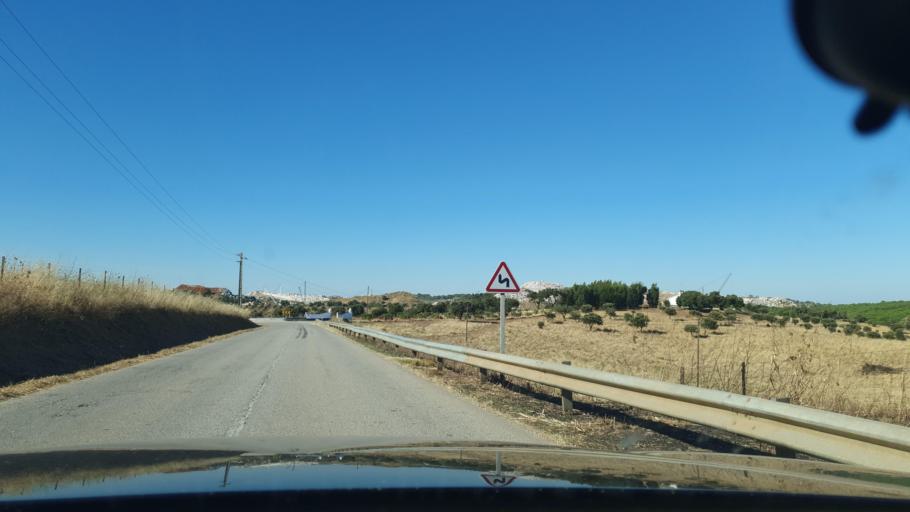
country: PT
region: Evora
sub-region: Alandroal
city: Alandroal
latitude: 38.7269
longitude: -7.4052
